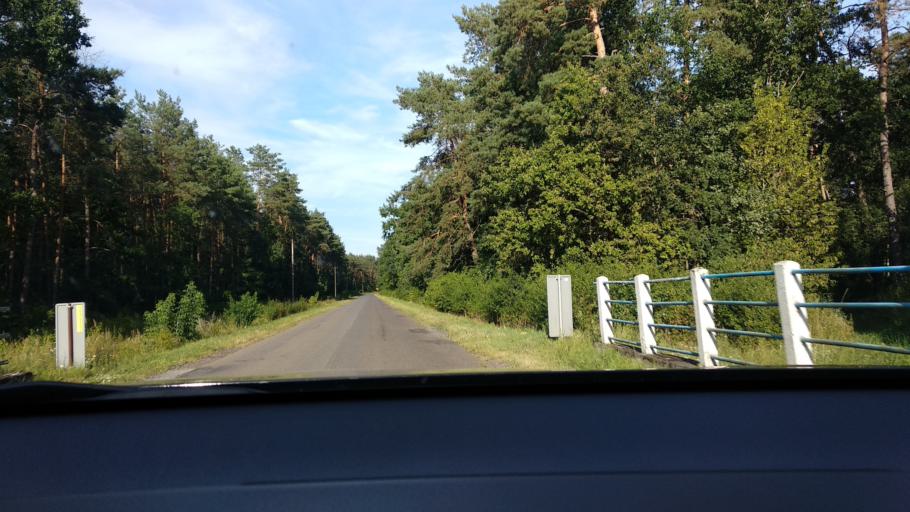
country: PL
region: Masovian Voivodeship
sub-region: Powiat pultuski
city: Pultusk
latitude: 52.7115
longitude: 21.1463
